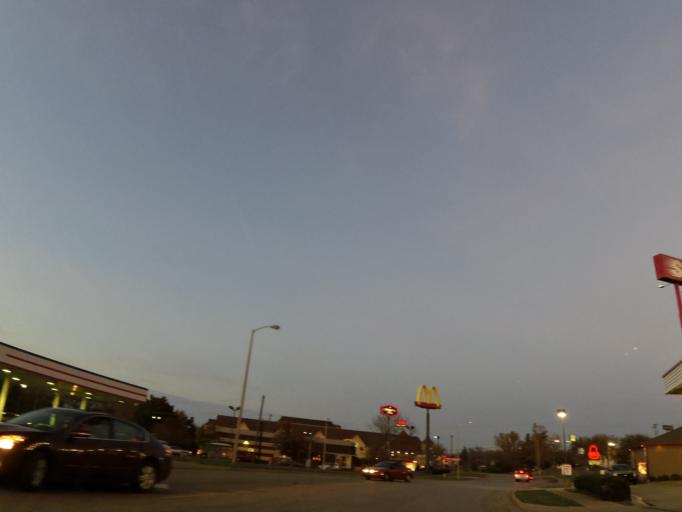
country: US
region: Kentucky
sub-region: Fayette County
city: Lexington-Fayette
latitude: 38.0415
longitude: -84.4244
